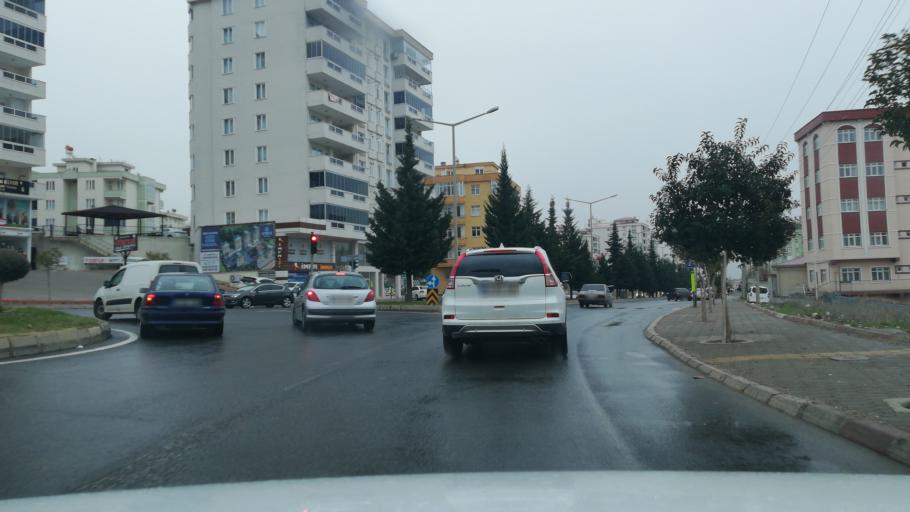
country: TR
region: Kahramanmaras
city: Kahramanmaras
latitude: 37.5913
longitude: 36.8826
